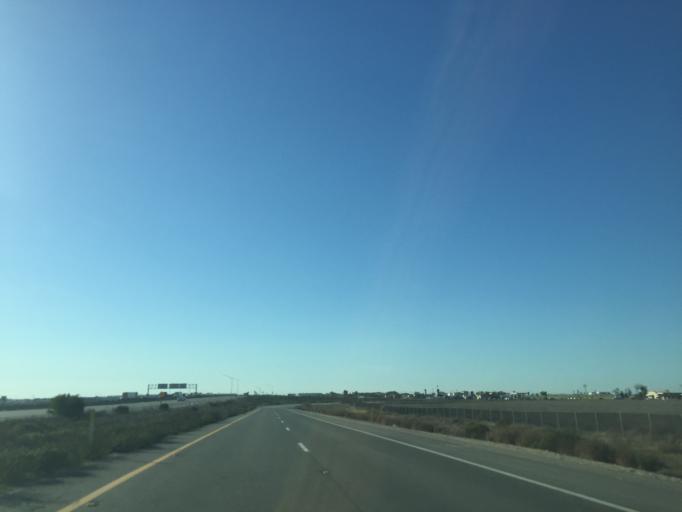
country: MX
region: Baja California
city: Tijuana
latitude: 32.5647
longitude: -116.9554
